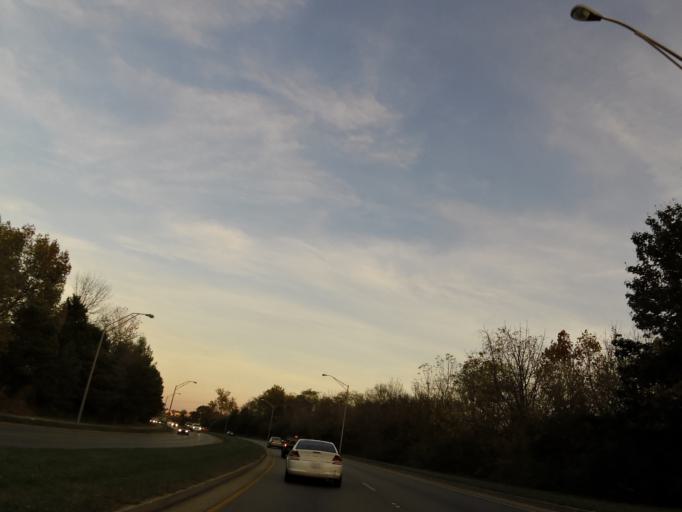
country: US
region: Kentucky
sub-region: Fayette County
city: Lexington
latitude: 37.9677
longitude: -84.5076
